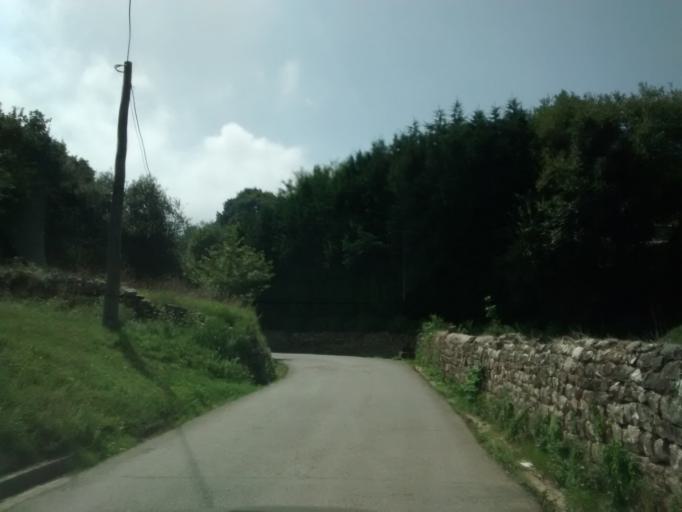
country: ES
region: Cantabria
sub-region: Provincia de Cantabria
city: Ruente
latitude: 43.2568
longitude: -4.2466
